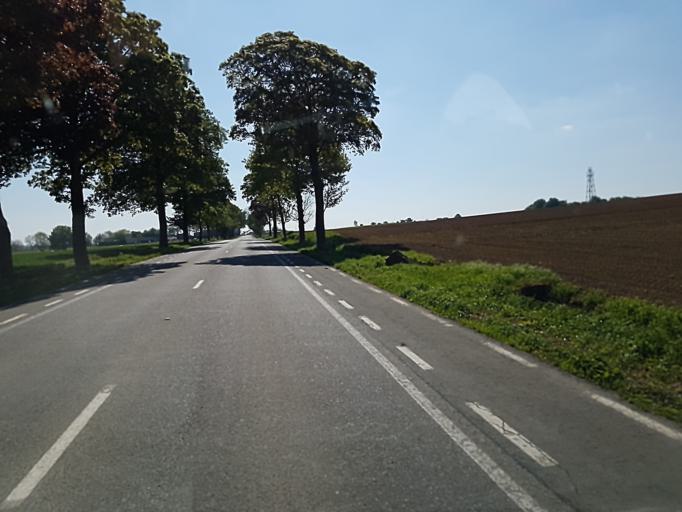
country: BE
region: Wallonia
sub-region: Province du Hainaut
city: Chievres
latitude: 50.5989
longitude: 3.8227
